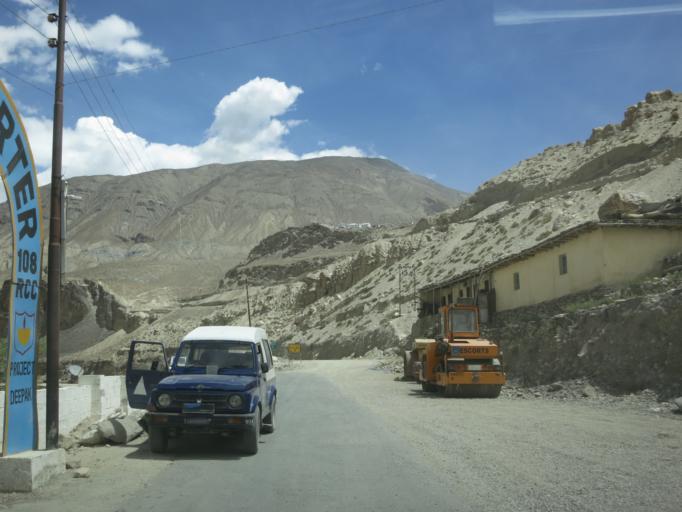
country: CN
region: Tibet Autonomous Region
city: Diyag
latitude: 32.0525
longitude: 78.6070
